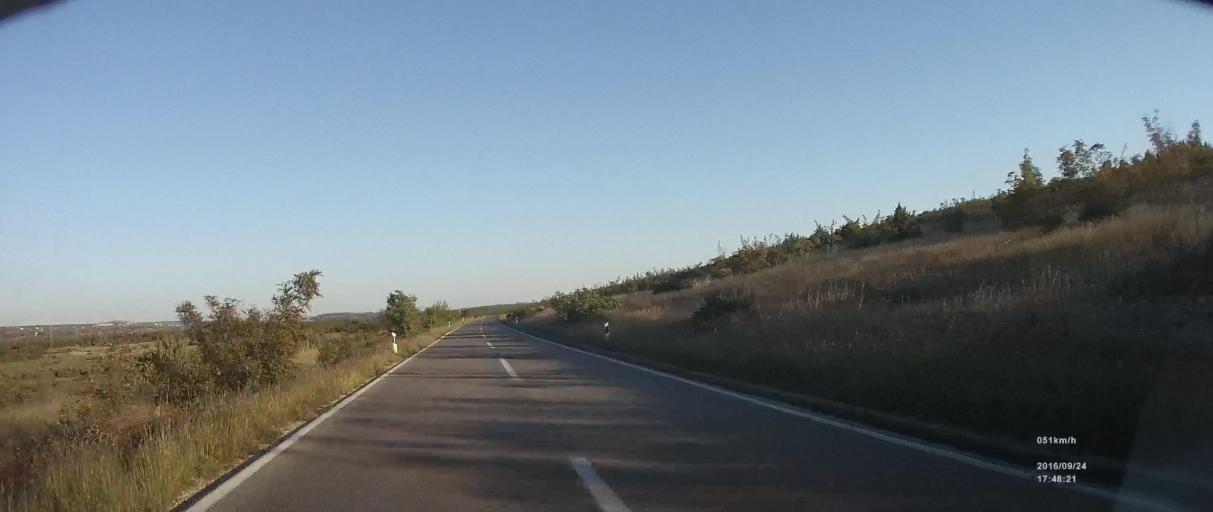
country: HR
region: Zadarska
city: Polaca
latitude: 44.0653
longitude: 15.5358
